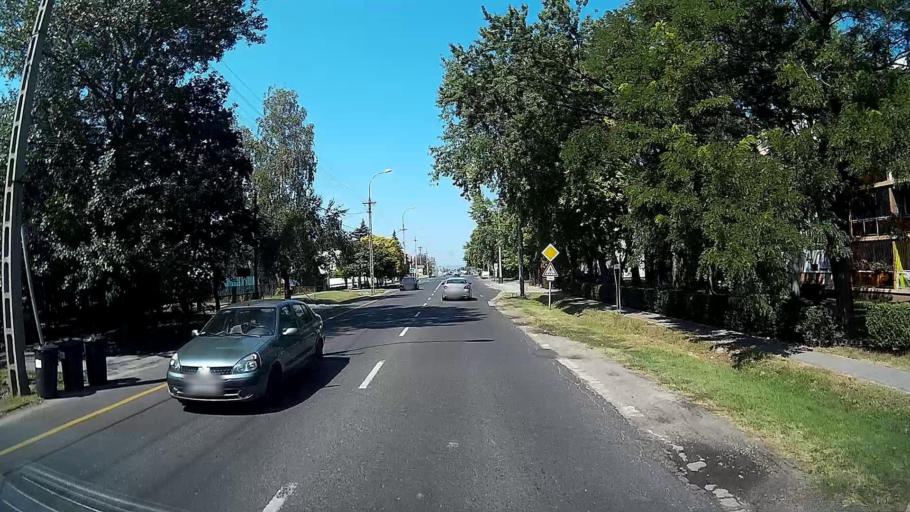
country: HU
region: Pest
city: Vecses
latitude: 47.4156
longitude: 19.2585
